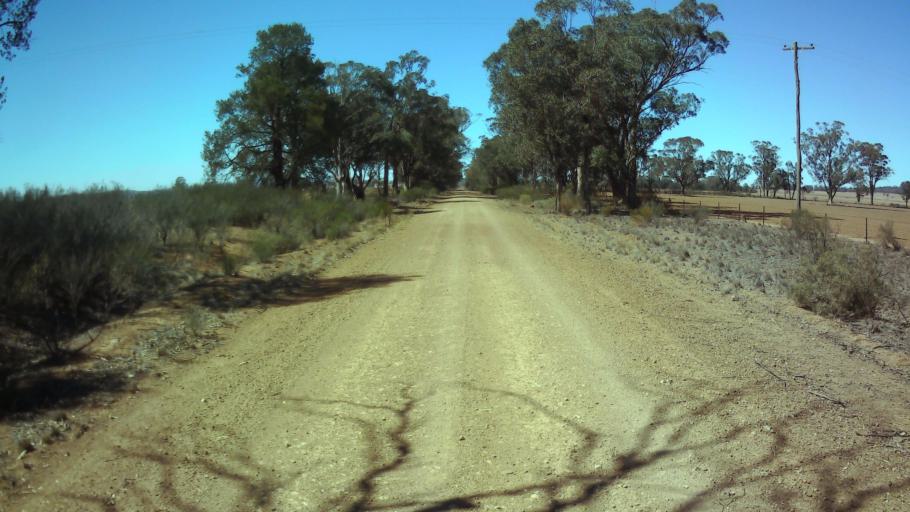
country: AU
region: New South Wales
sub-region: Weddin
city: Grenfell
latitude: -33.7097
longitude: 147.9707
